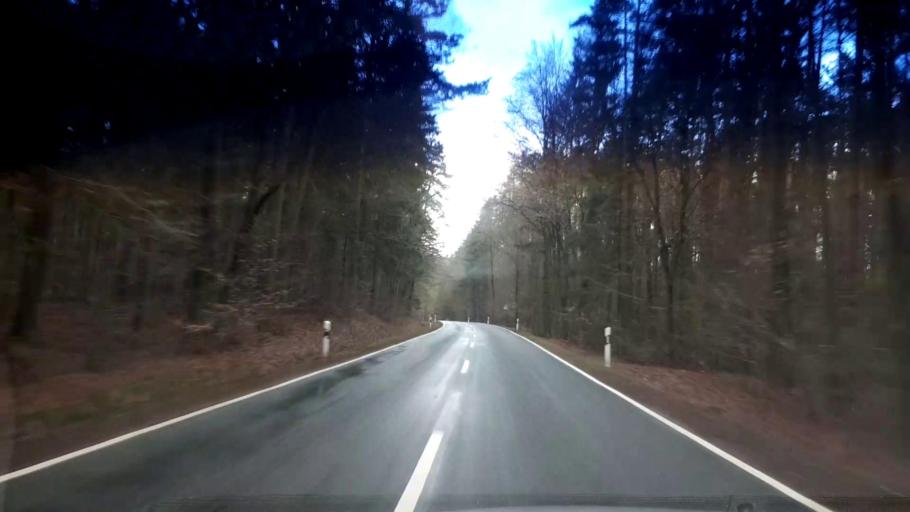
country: DE
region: Bavaria
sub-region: Upper Franconia
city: Lauter
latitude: 49.9653
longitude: 10.7612
